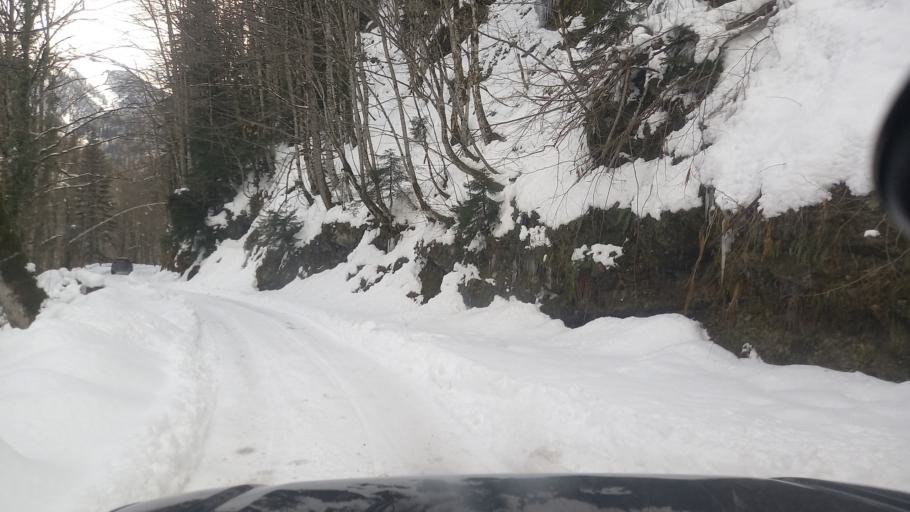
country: GE
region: Abkhazia
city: Gagra
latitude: 43.4791
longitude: 40.5580
